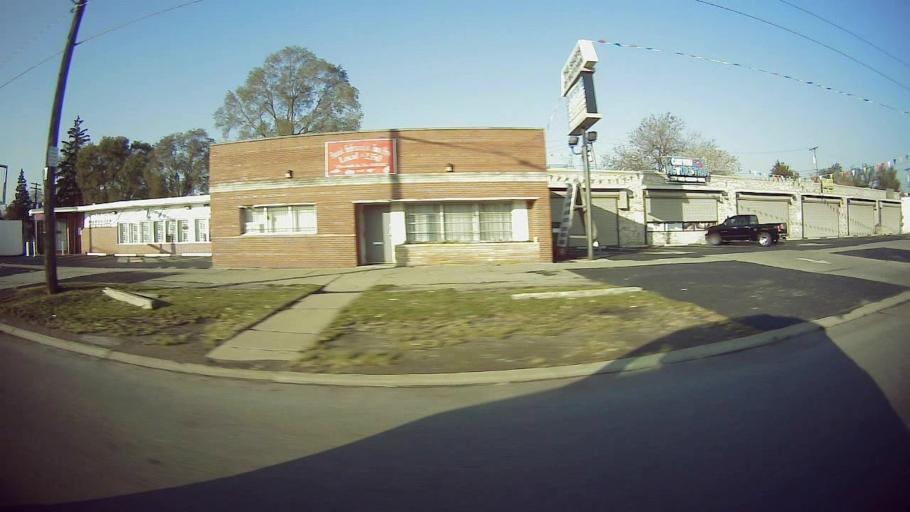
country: US
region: Michigan
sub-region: Oakland County
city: Oak Park
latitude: 42.3908
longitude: -83.1984
